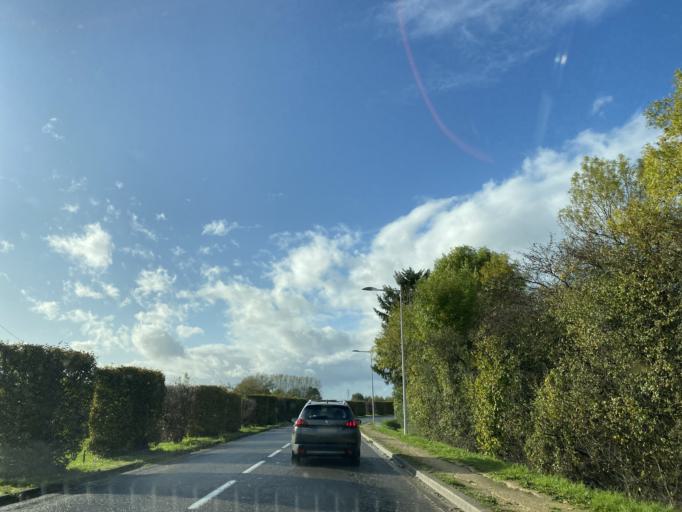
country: FR
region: Centre
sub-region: Departement du Cher
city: Bourges
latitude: 47.0930
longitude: 2.3816
